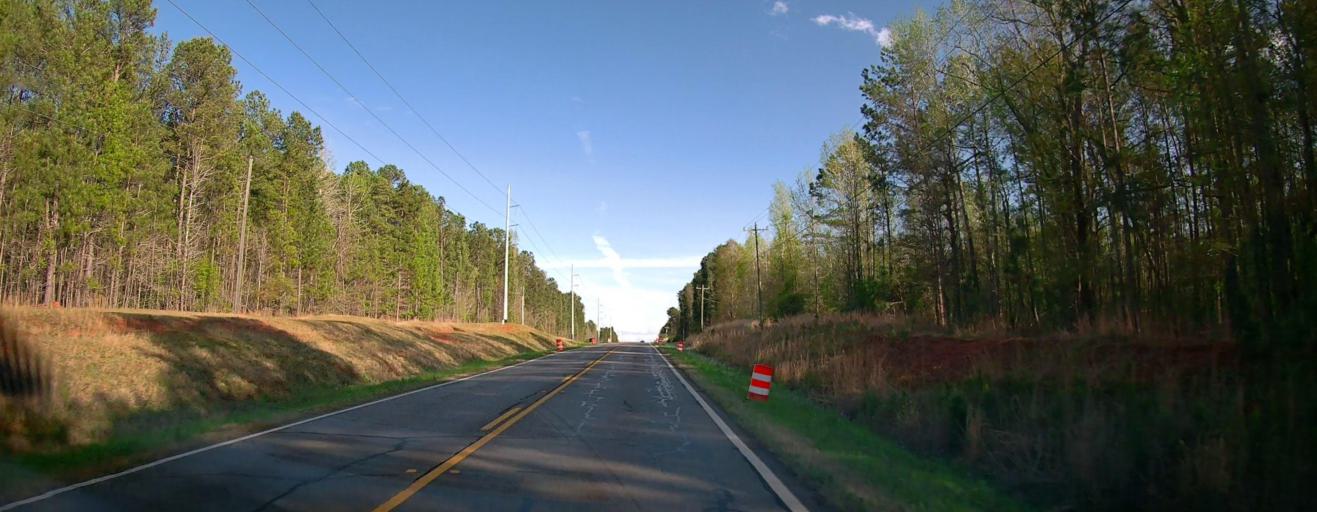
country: US
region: Georgia
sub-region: Baldwin County
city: Milledgeville
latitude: 33.1337
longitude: -83.3233
